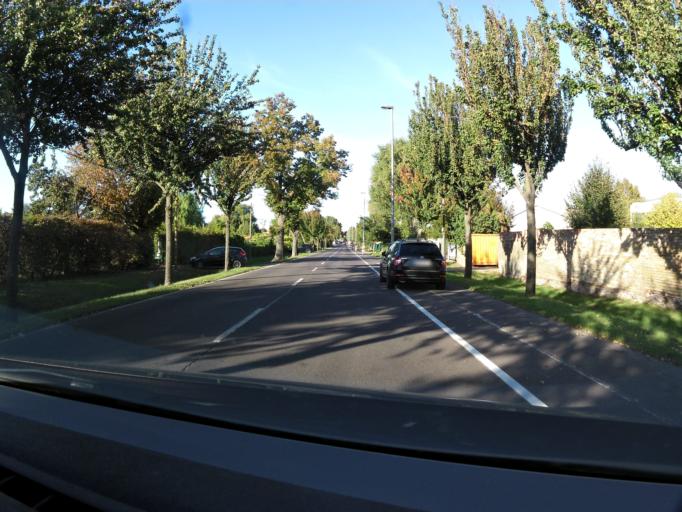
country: DE
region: Saxony-Anhalt
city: Diesdorf
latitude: 52.0839
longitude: 11.5645
